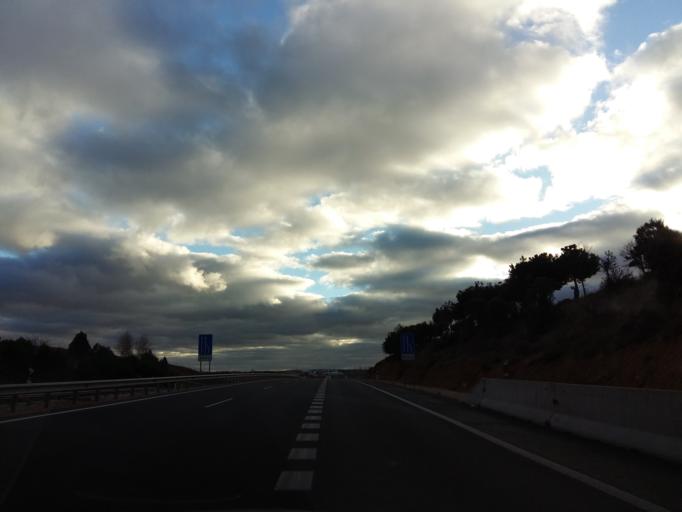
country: ES
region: Castille and Leon
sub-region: Provincia de Burgos
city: Cogollos
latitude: 42.1911
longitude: -3.6982
